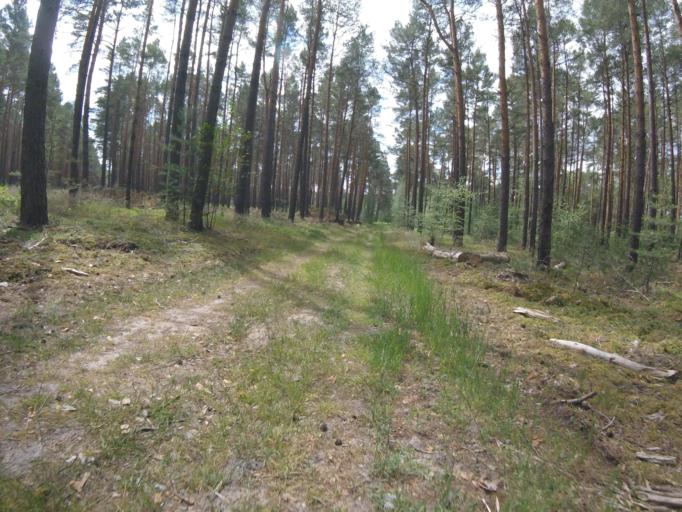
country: DE
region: Brandenburg
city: Halbe
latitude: 52.1094
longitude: 13.6636
